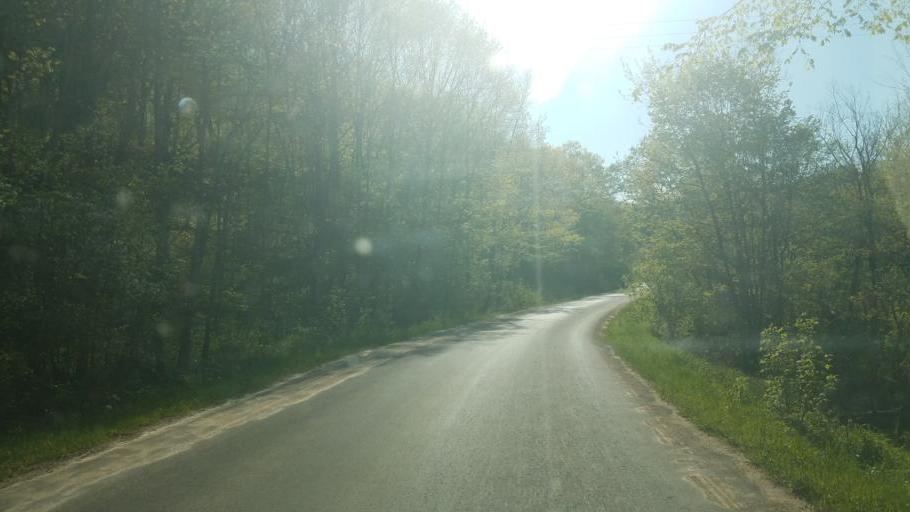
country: US
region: Wisconsin
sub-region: Vernon County
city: Hillsboro
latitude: 43.6276
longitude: -90.4614
